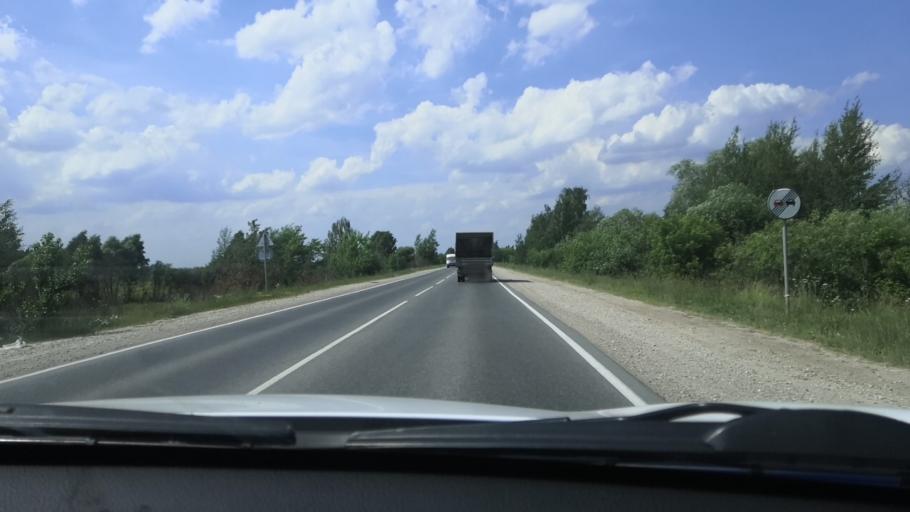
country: RU
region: Rjazan
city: Murmino
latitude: 54.6349
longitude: 39.9477
